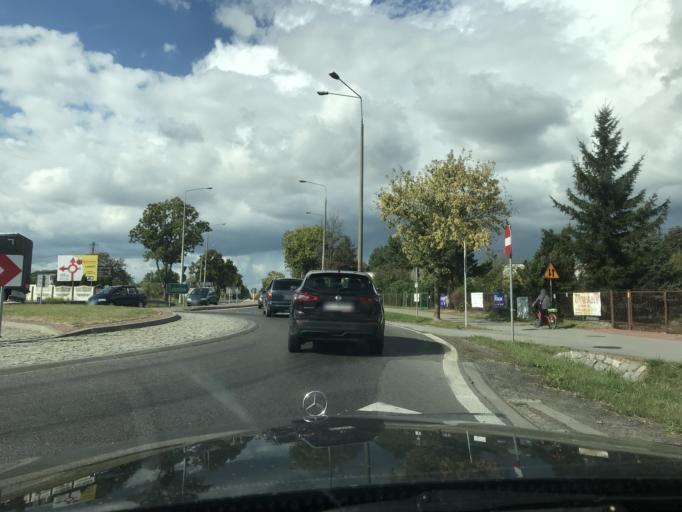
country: PL
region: Lublin Voivodeship
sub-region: Powiat lubartowski
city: Lubartow
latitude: 51.4360
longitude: 22.6251
